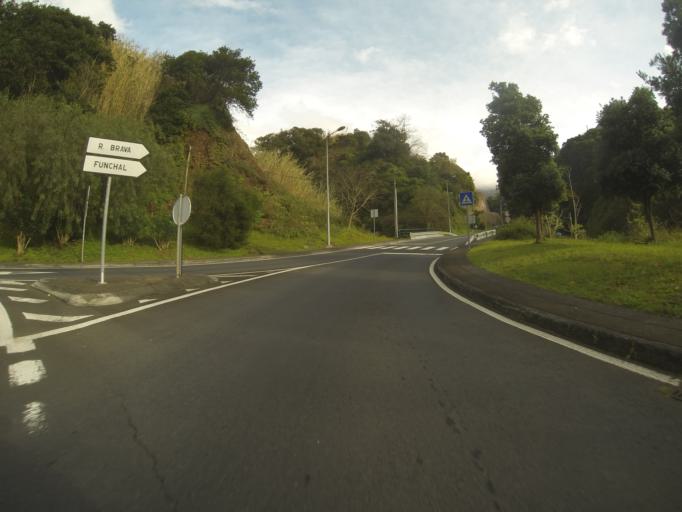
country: PT
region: Madeira
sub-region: Sao Vicente
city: Sao Vicente
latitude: 32.7918
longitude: -17.0343
